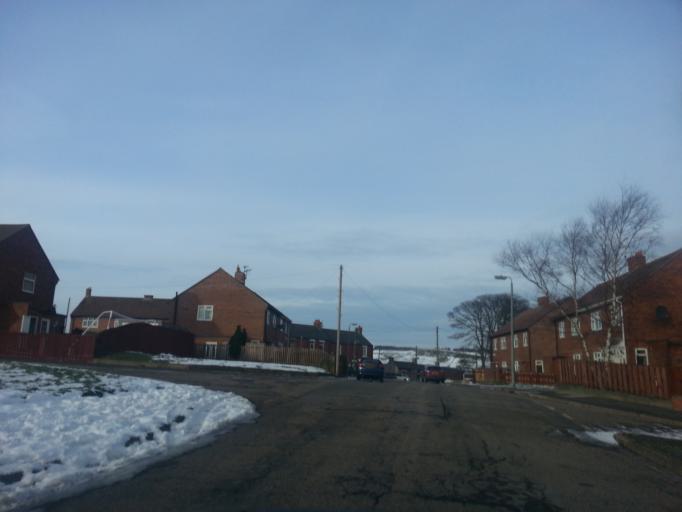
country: GB
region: England
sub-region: County Durham
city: Crook
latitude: 54.7171
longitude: -1.7581
